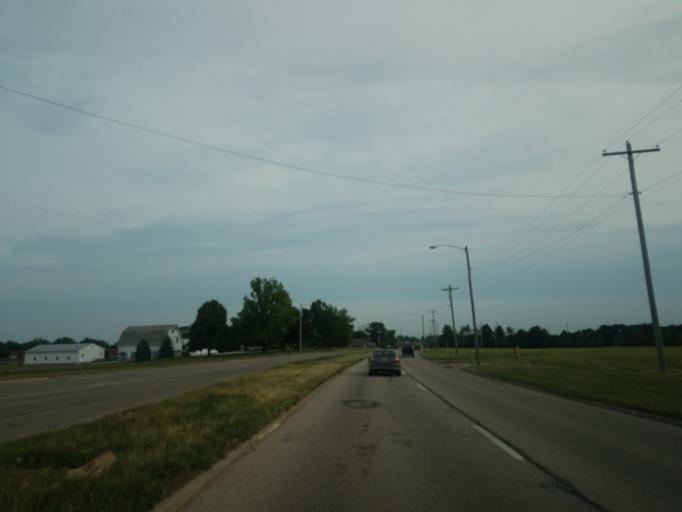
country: US
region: Illinois
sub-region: McLean County
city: Bloomington
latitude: 40.4511
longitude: -88.9923
